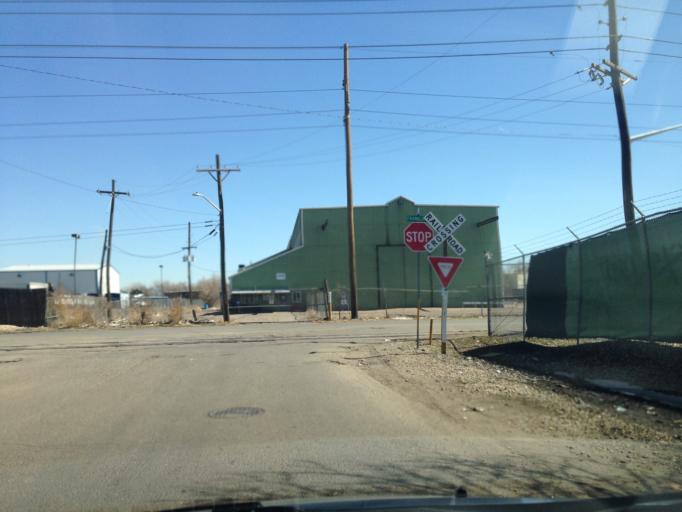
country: US
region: Colorado
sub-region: Adams County
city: Commerce City
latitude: 39.7955
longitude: -104.9691
